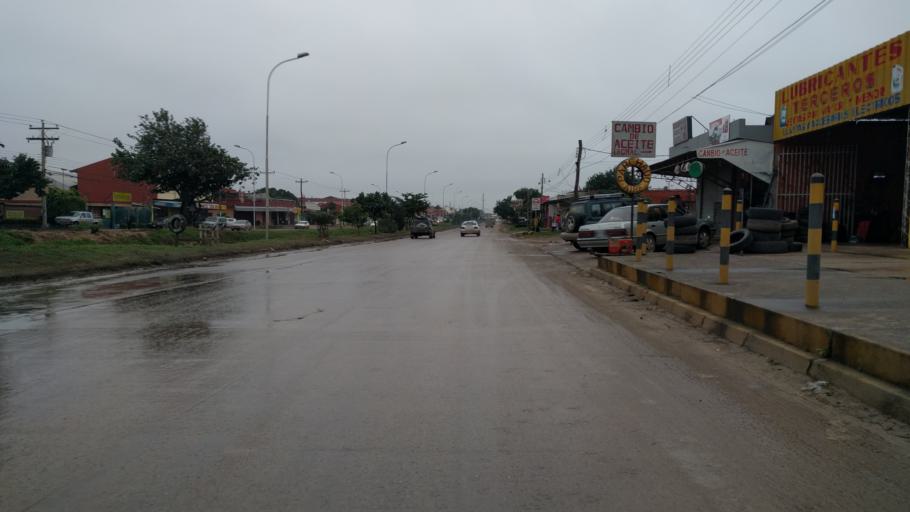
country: BO
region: Santa Cruz
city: Santa Cruz de la Sierra
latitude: -17.8310
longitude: -63.1762
